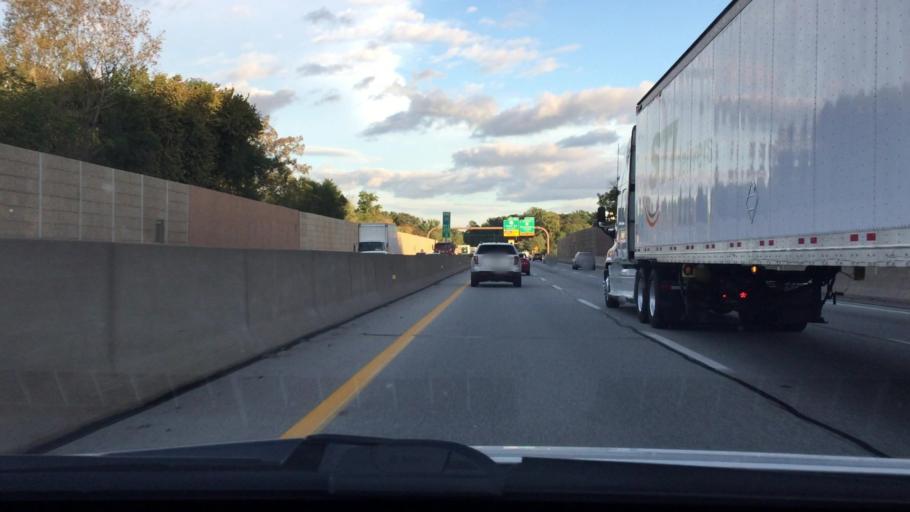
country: US
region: Pennsylvania
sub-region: Bucks County
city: Feasterville
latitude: 40.1391
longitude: -74.9963
